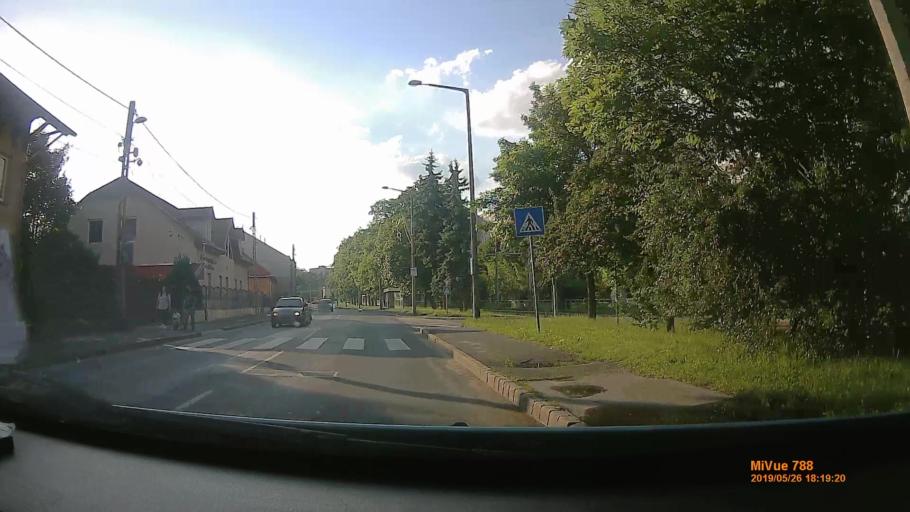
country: HU
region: Borsod-Abauj-Zemplen
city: Sajobabony
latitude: 48.1041
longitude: 20.6835
